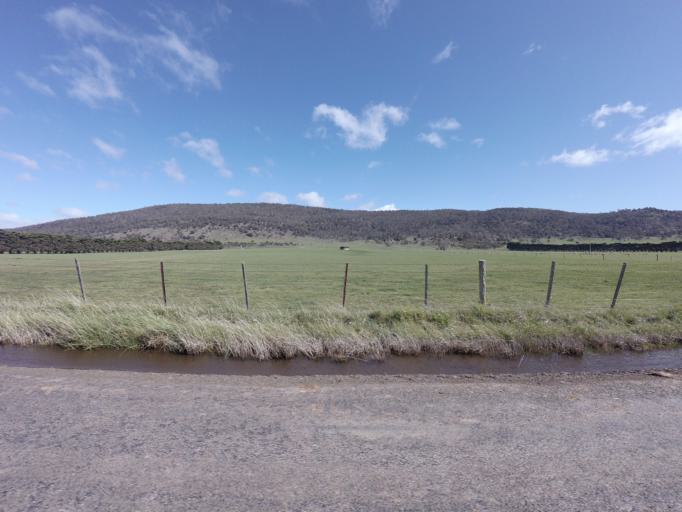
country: AU
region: Tasmania
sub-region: Northern Midlands
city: Evandale
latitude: -41.9648
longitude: 147.4403
